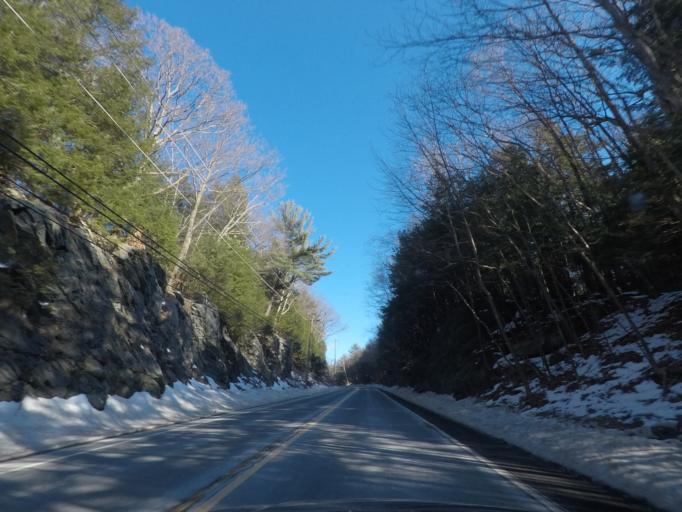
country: US
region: New York
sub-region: Columbia County
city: Chatham
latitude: 42.3195
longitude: -73.5178
